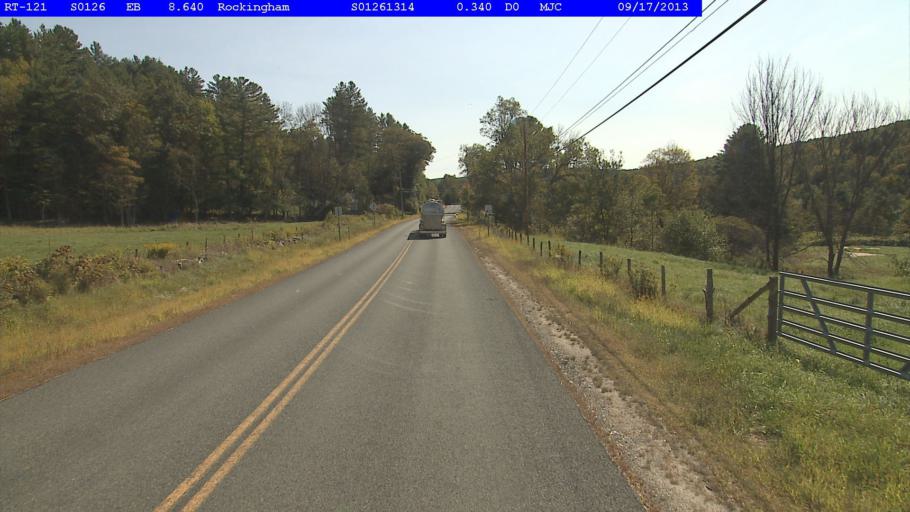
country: US
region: Vermont
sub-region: Windham County
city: Rockingham
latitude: 43.1487
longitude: -72.5525
